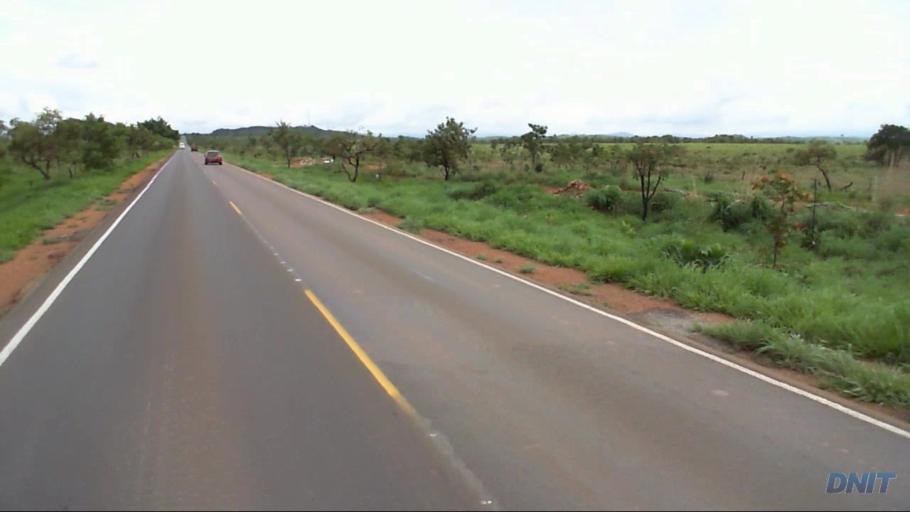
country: BR
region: Goias
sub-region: Padre Bernardo
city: Padre Bernardo
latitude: -15.2423
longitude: -48.2716
